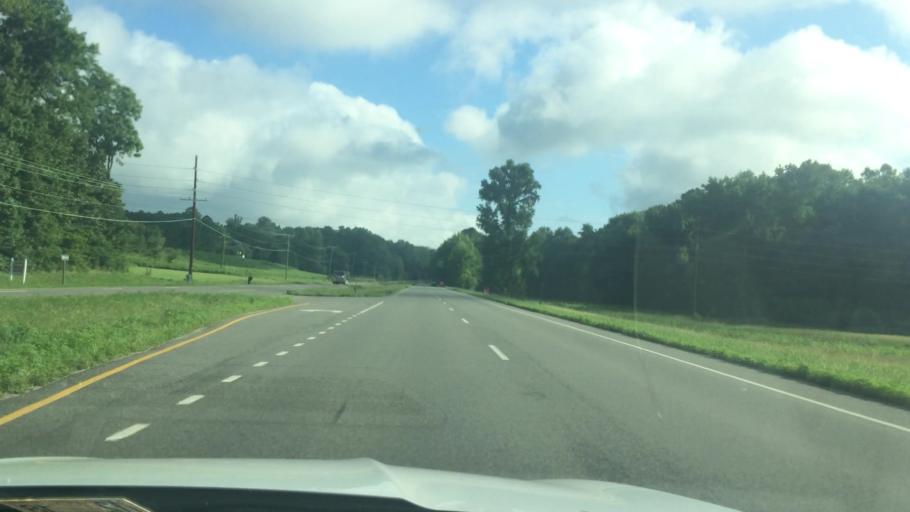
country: US
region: Virginia
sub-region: Gloucester County
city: Gloucester Courthouse
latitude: 37.4442
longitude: -76.4742
